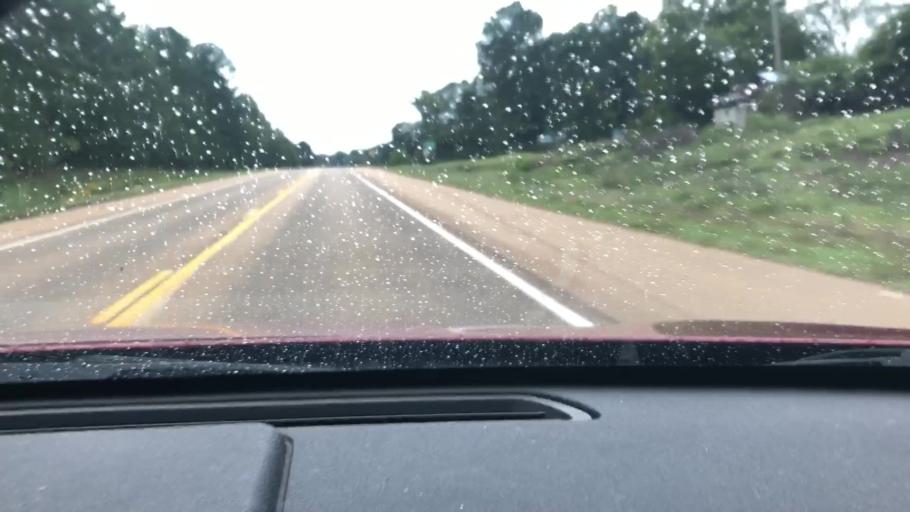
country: US
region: Arkansas
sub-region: Lafayette County
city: Stamps
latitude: 33.3590
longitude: -93.4212
